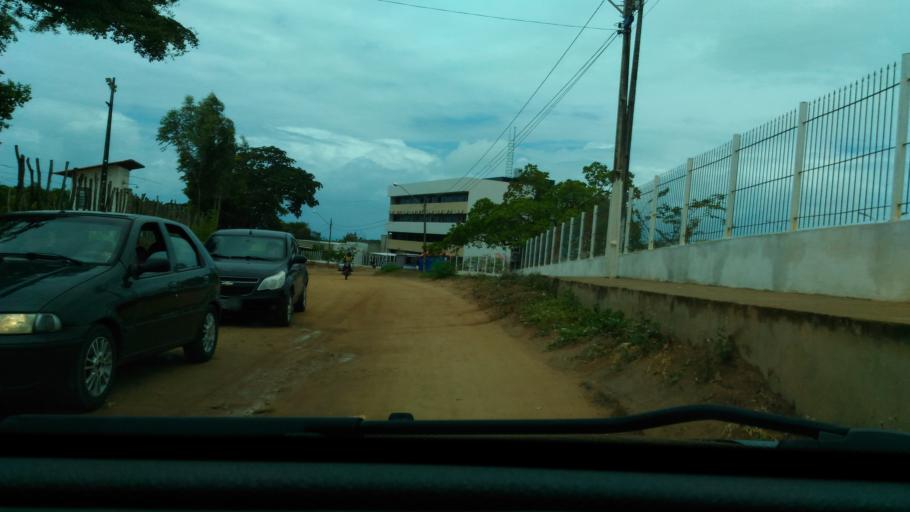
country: BR
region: Paraiba
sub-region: Joao Pessoa
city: Joao Pessoa
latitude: -7.1618
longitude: -34.8183
